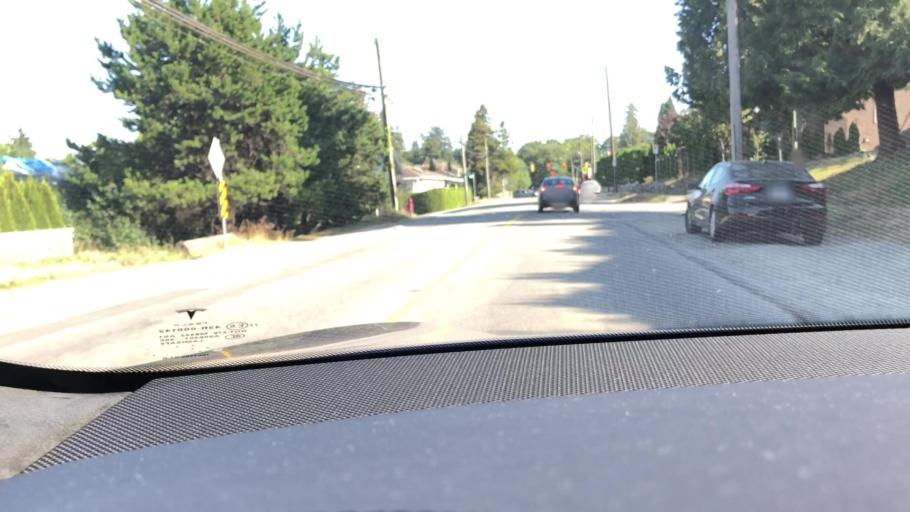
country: CA
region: British Columbia
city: Burnaby
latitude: 49.2512
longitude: -122.9815
